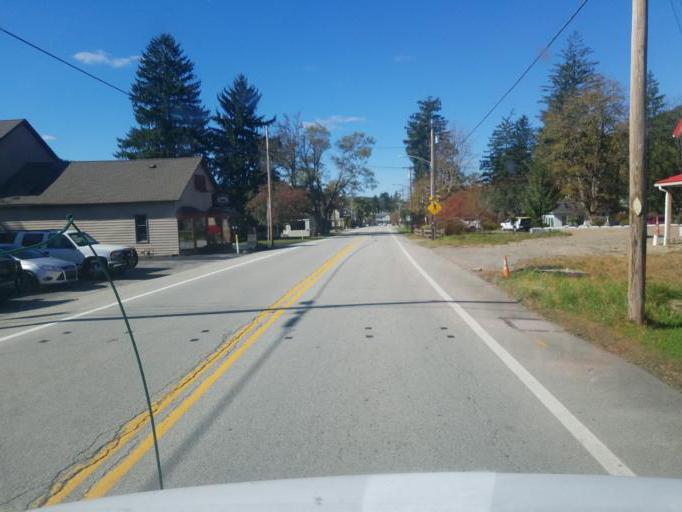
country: US
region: Pennsylvania
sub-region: Westmoreland County
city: Ligonier
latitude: 40.2111
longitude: -79.1965
